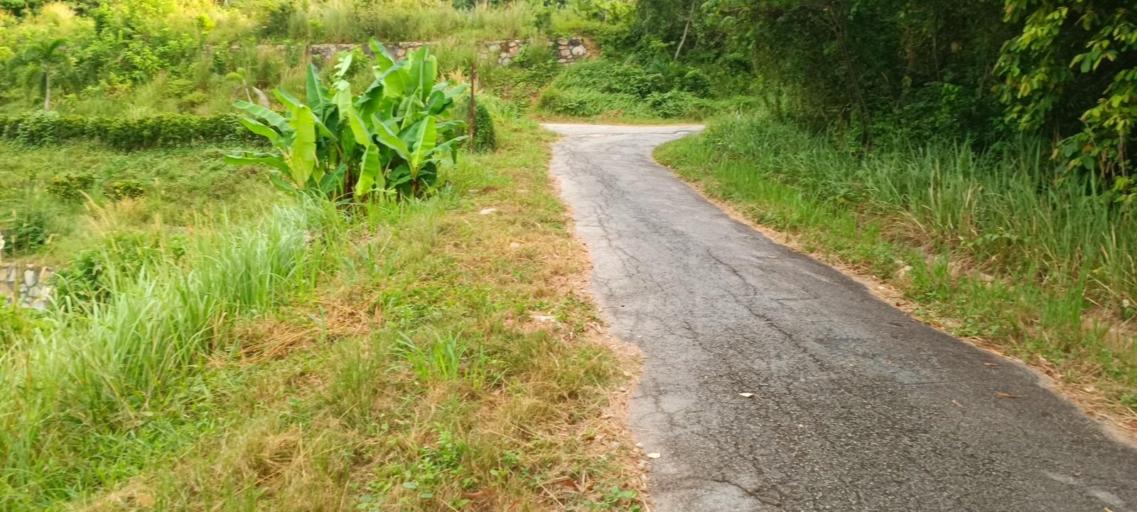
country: MY
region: Penang
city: Juru
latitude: 5.2672
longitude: 100.4185
